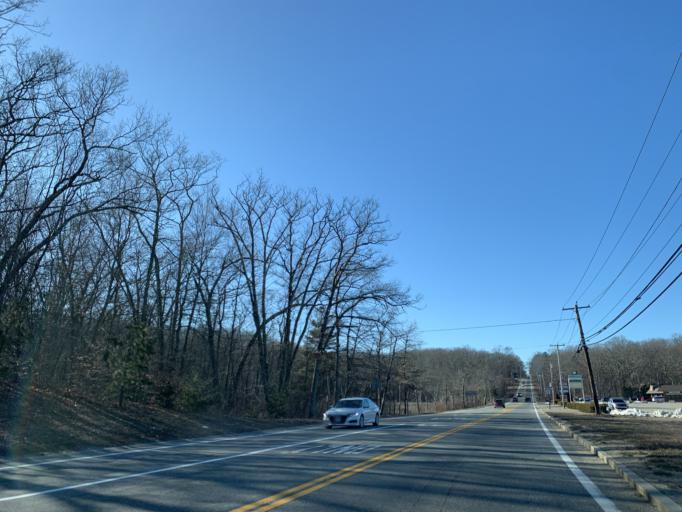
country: US
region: Rhode Island
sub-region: Providence County
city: North Providence
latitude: 41.8796
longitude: -71.4744
